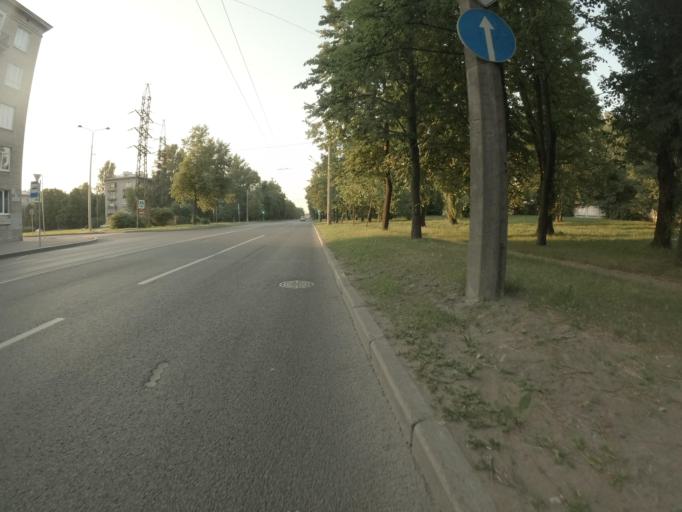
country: RU
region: St.-Petersburg
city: Avtovo
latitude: 59.8726
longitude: 30.2743
